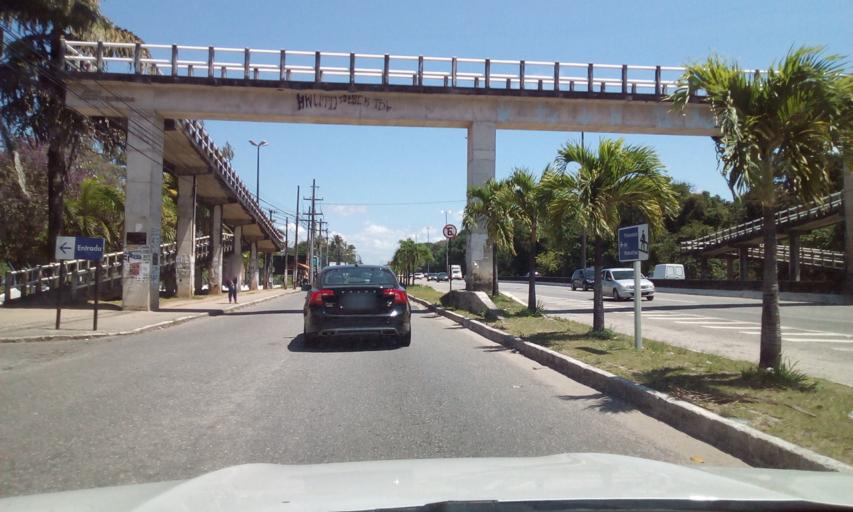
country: BR
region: Paraiba
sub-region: Joao Pessoa
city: Joao Pessoa
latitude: -7.1578
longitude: -34.8581
